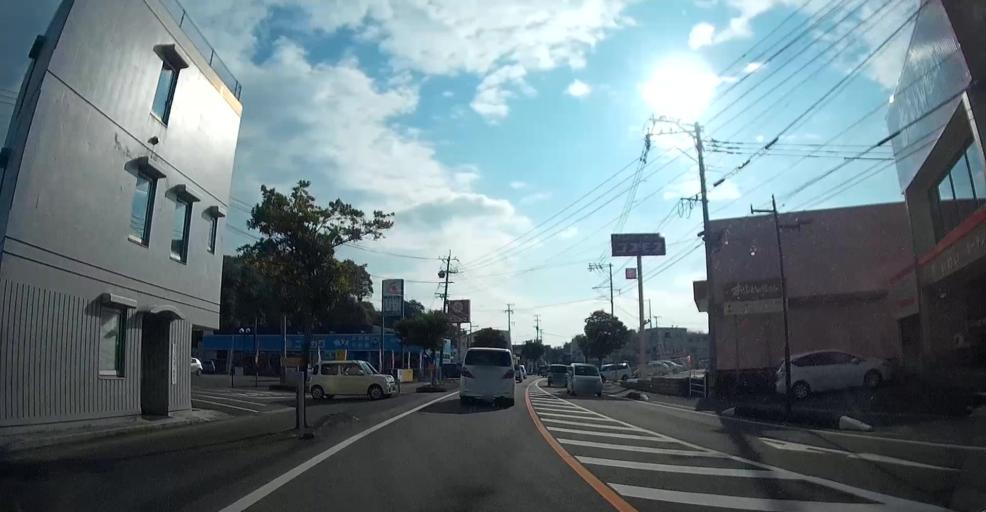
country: JP
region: Kumamoto
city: Yatsushiro
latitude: 32.5852
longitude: 130.4295
